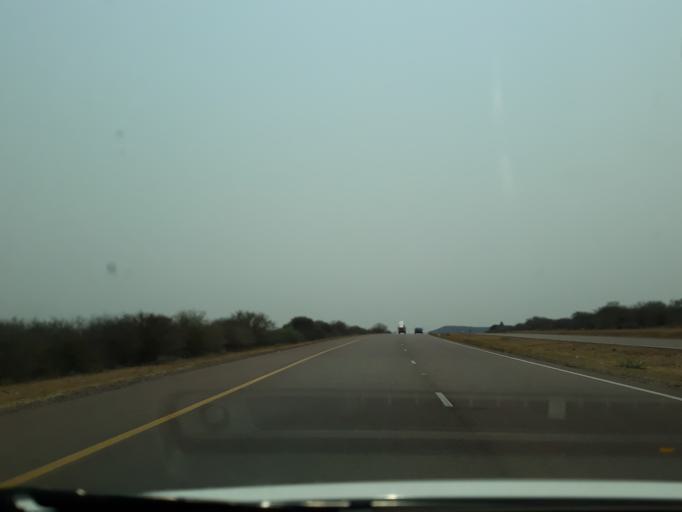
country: BW
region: Kgatleng
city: Bokaa
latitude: -24.4157
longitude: 26.0489
